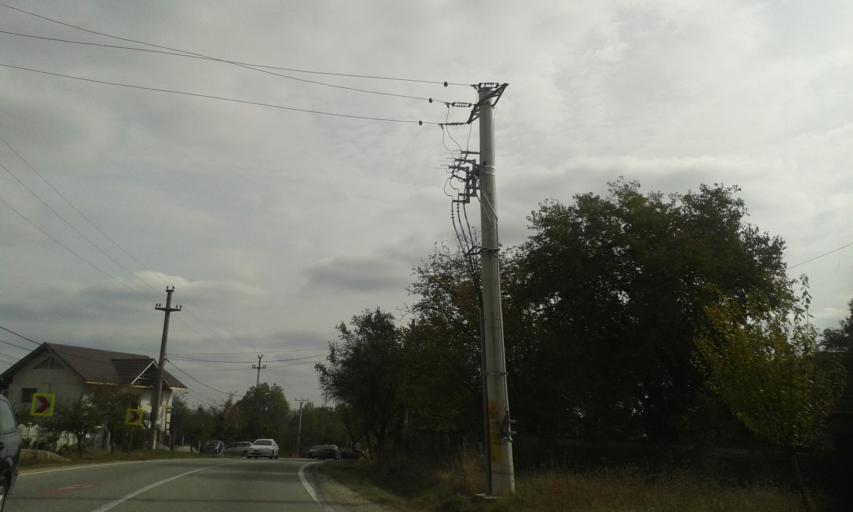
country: RO
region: Gorj
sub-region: Comuna Scoarta
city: Scoarta
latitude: 45.0263
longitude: 23.4354
